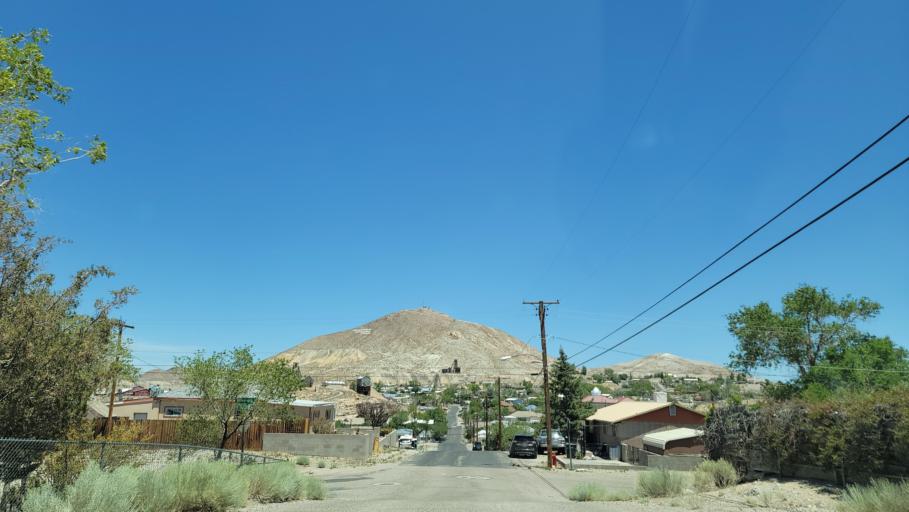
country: US
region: Nevada
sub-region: Nye County
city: Tonopah
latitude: 38.0635
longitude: -117.2301
